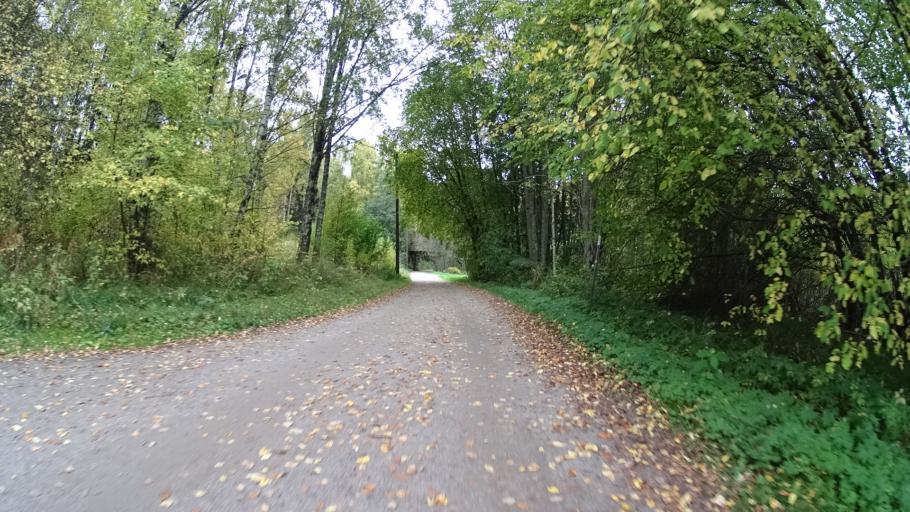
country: FI
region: Uusimaa
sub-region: Helsinki
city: Vantaa
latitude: 60.2100
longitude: 25.0289
